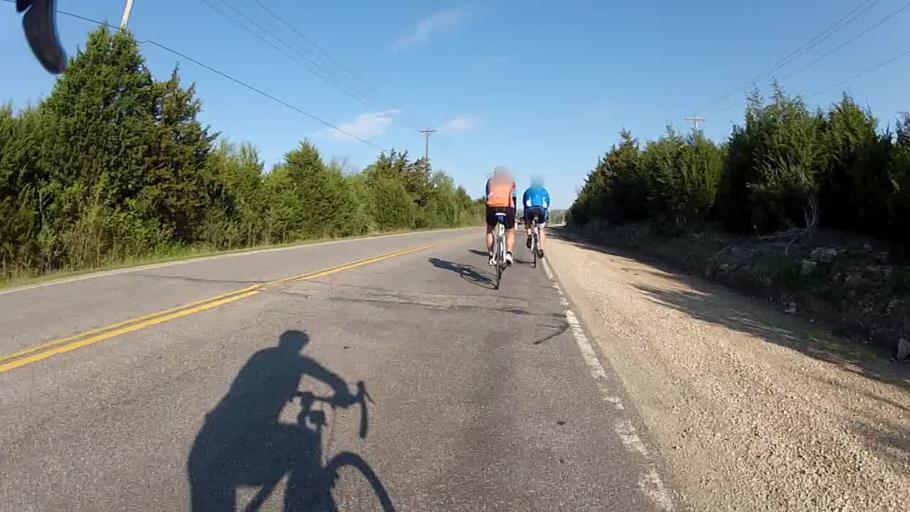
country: US
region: Kansas
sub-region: Riley County
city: Manhattan
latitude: 39.1896
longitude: -96.6373
